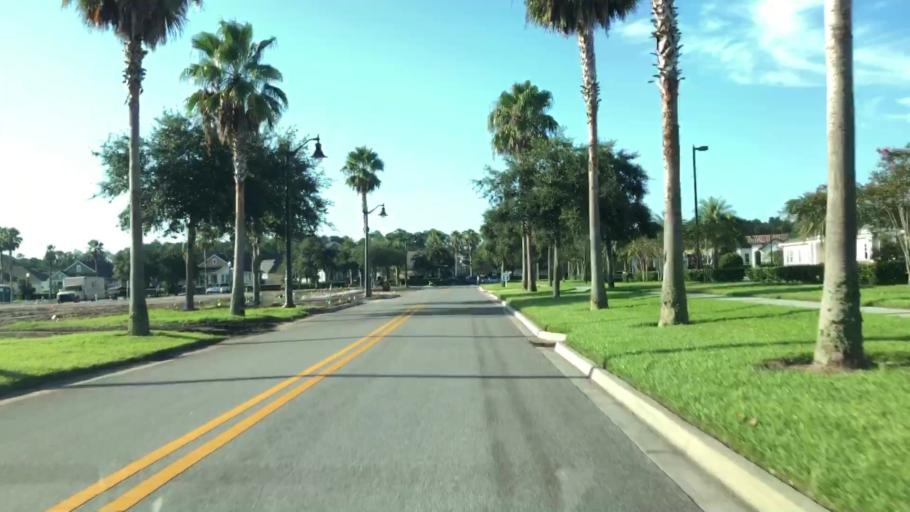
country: US
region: Florida
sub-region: Saint Johns County
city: Palm Valley
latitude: 30.1094
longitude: -81.4210
